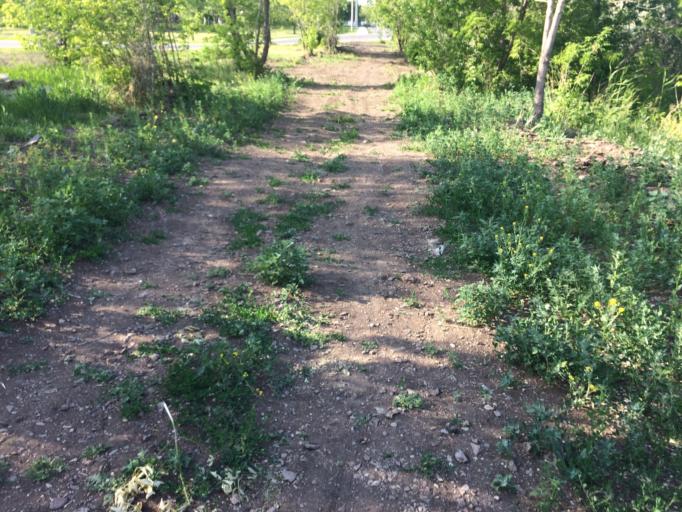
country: RU
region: Chelyabinsk
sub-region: Gorod Magnitogorsk
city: Magnitogorsk
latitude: 53.4009
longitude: 58.9947
